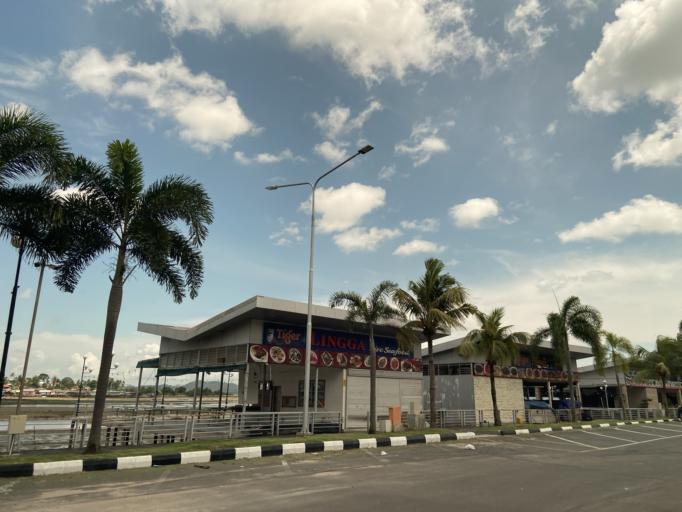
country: SG
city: Singapore
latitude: 1.1525
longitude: 103.9987
